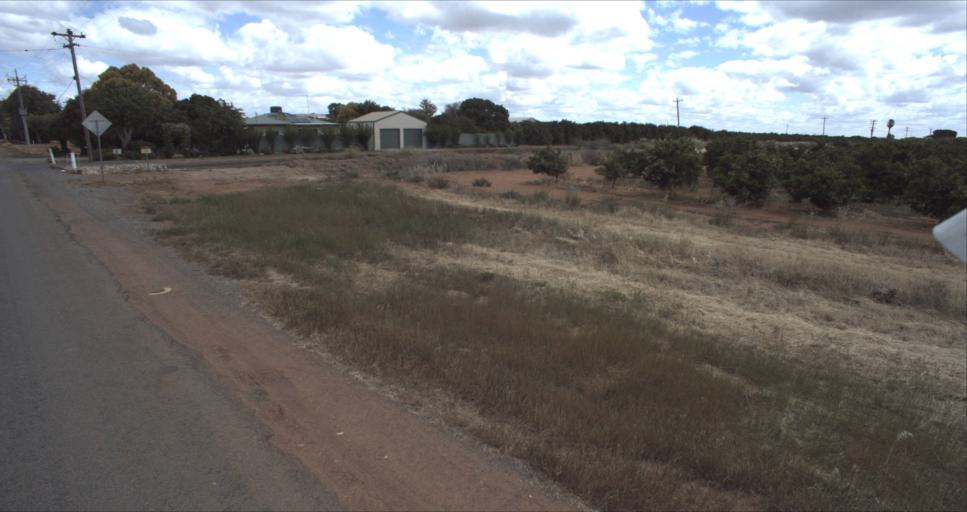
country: AU
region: New South Wales
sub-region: Leeton
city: Leeton
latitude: -34.5803
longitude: 146.3970
